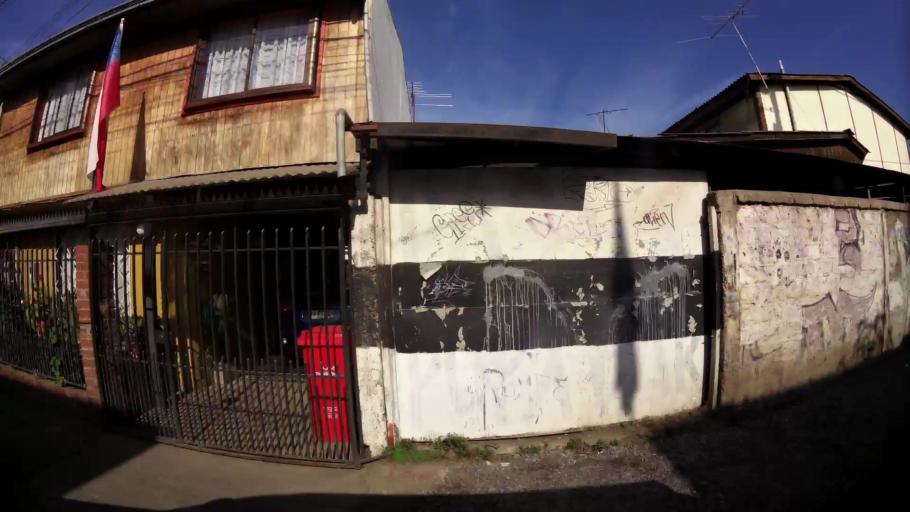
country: CL
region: Santiago Metropolitan
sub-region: Provincia de Talagante
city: Talagante
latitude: -33.6726
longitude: -70.9385
